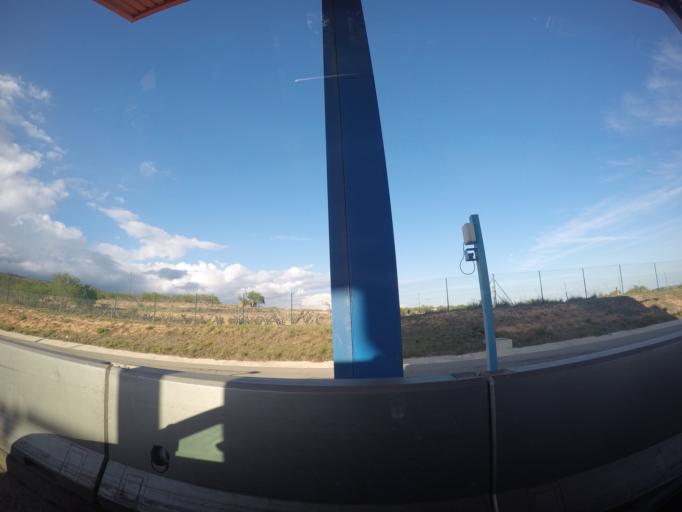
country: ES
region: Catalonia
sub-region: Provincia de Tarragona
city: la Bisbal del Penedes
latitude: 41.2804
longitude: 1.4984
